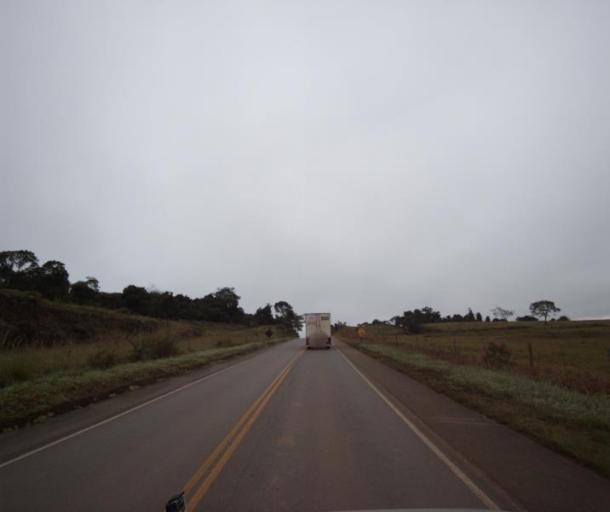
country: BR
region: Goias
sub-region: Pirenopolis
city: Pirenopolis
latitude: -15.9582
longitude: -48.8132
